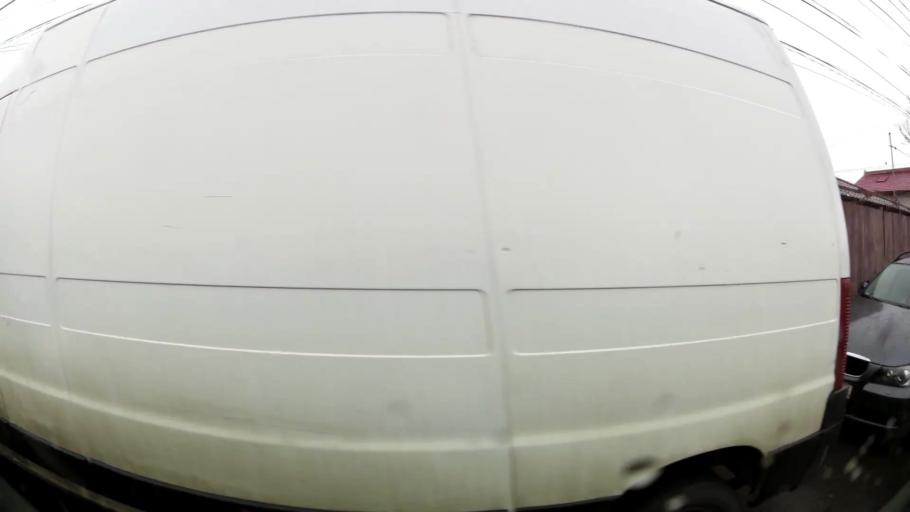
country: RO
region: Ilfov
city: Dobroesti
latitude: 44.4211
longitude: 26.1834
